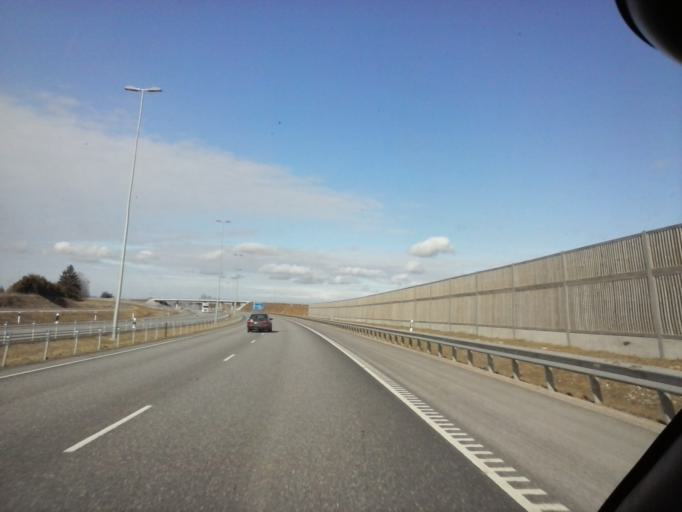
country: EE
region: Harju
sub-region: Raasiku vald
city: Arukula
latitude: 59.1821
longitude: 25.1316
